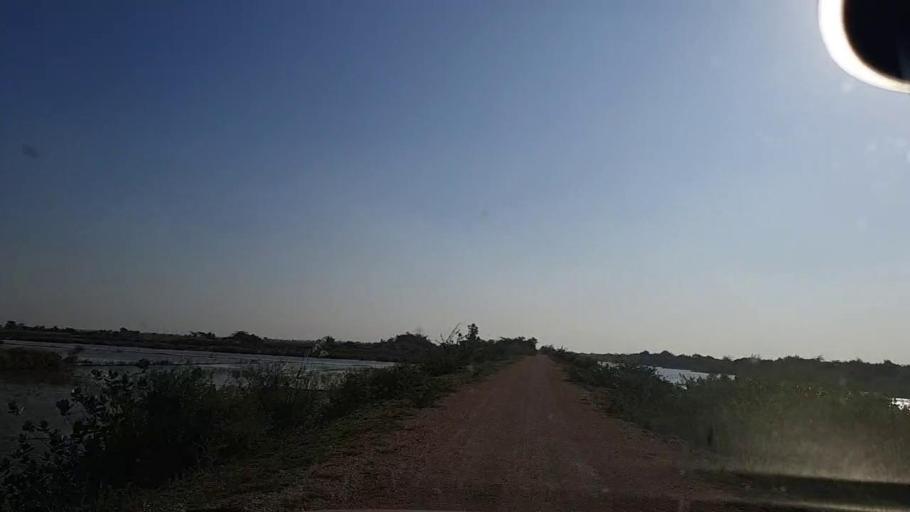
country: PK
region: Sindh
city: Chuhar Jamali
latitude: 24.5587
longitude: 68.0387
